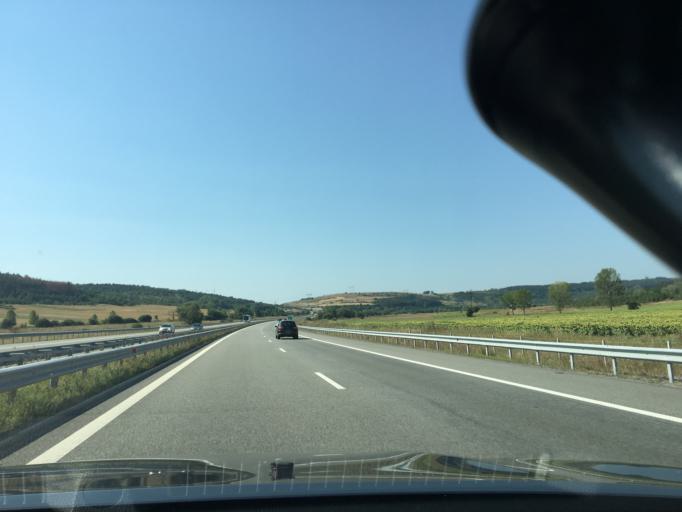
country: BG
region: Kyustendil
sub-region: Obshtina Bobovdol
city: Bobovdol
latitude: 42.3940
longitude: 23.1196
